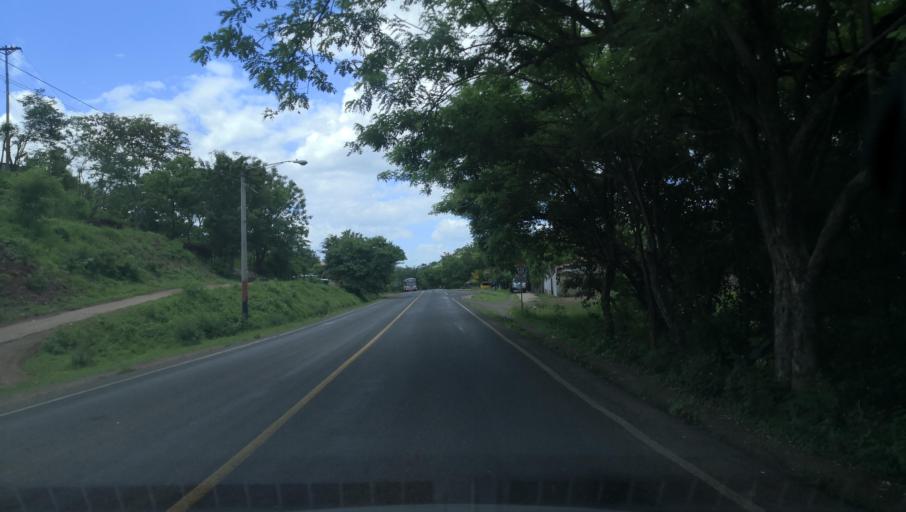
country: NI
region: Madriz
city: Palacaguina
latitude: 13.4108
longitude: -86.3999
